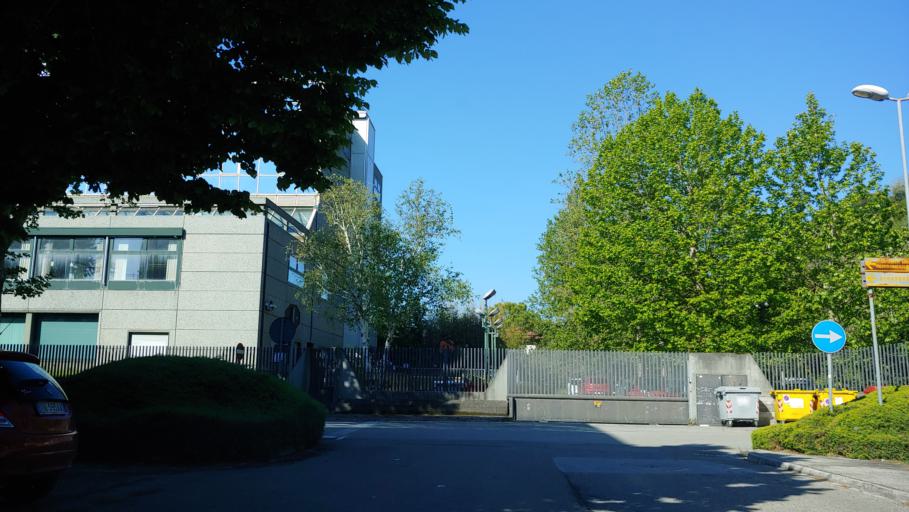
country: IT
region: The Marches
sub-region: Provincia di Pesaro e Urbino
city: Pesaro
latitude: 43.9073
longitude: 12.8636
